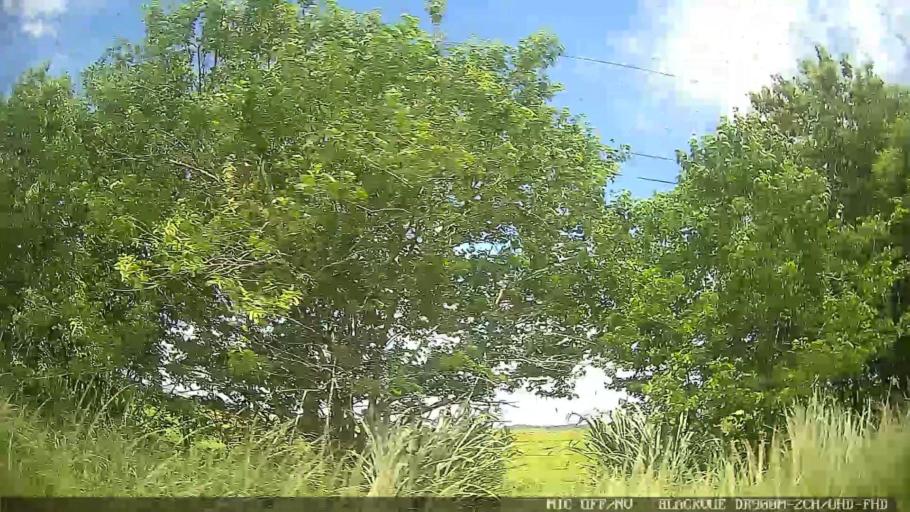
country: BR
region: Sao Paulo
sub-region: Conchas
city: Conchas
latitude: -23.0438
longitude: -48.0228
